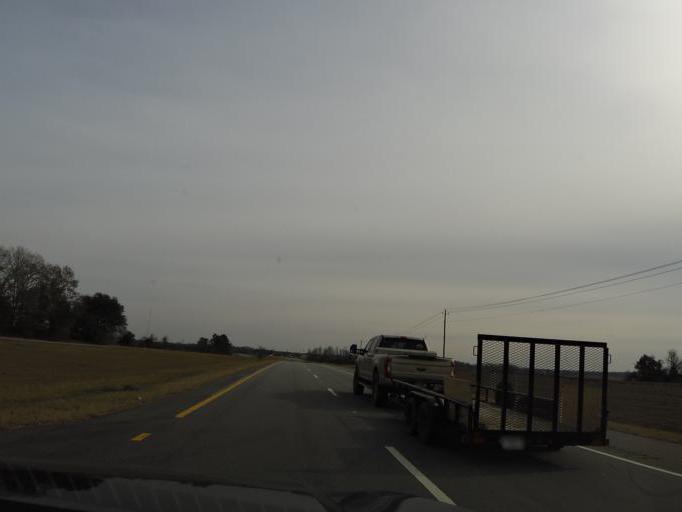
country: US
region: Georgia
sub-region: Seminole County
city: Donalsonville
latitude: 31.0961
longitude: -85.0031
